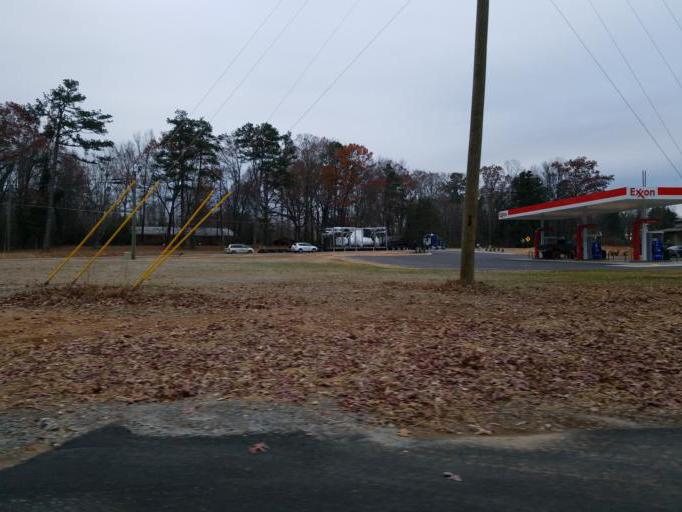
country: US
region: Georgia
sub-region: Dawson County
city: Dawsonville
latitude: 34.4419
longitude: -84.0945
